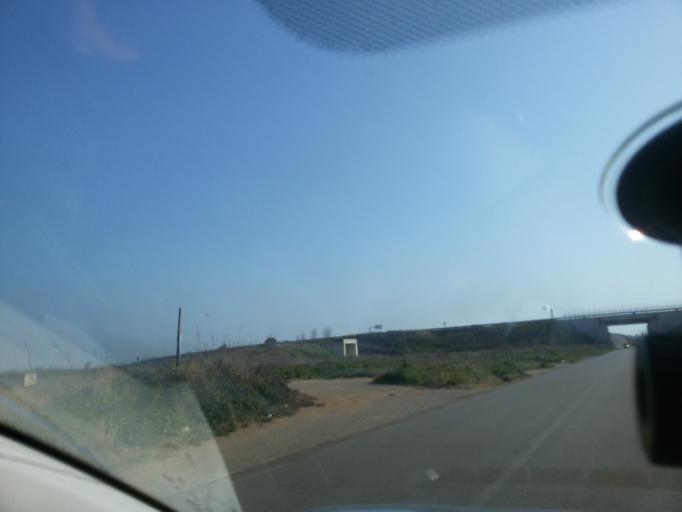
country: IT
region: Apulia
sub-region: Provincia di Brindisi
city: Mesagne
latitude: 40.5731
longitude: 17.8114
